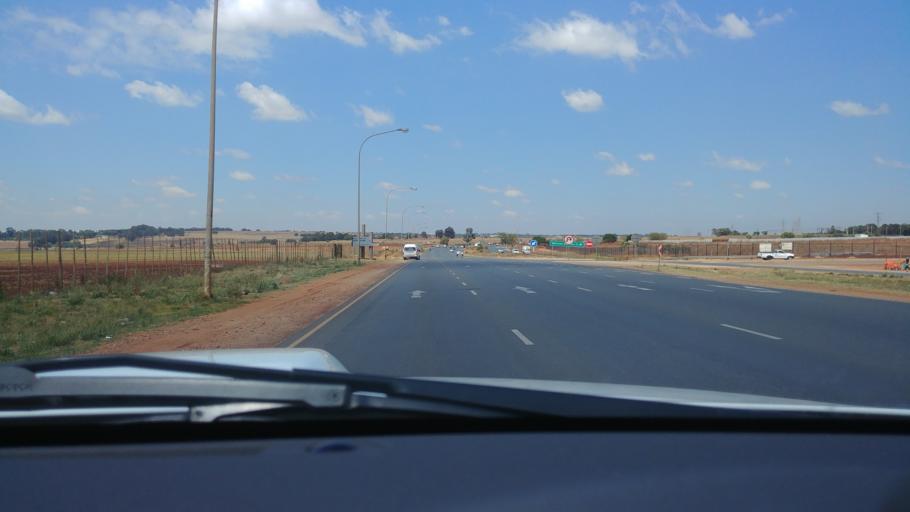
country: ZA
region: Gauteng
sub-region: Ekurhuleni Metropolitan Municipality
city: Tembisa
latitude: -26.0355
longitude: 28.2583
